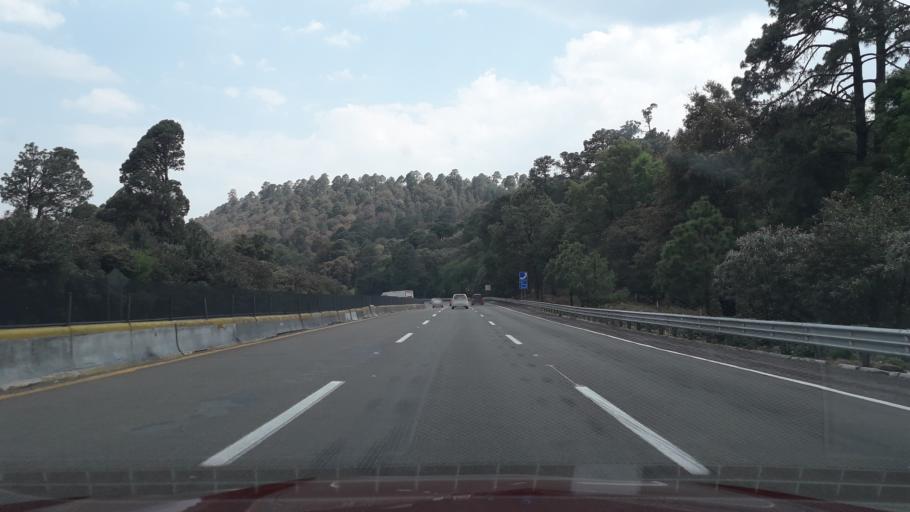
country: MX
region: Puebla
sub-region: Tlahuapan
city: Santa Cruz Otlatla
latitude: 19.3525
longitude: -98.6326
